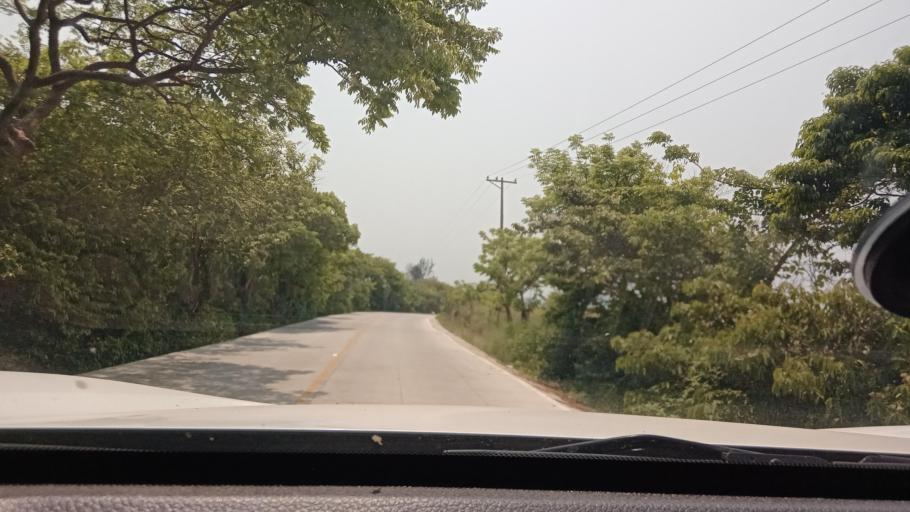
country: MX
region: Veracruz
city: Catemaco
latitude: 18.5567
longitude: -95.0047
